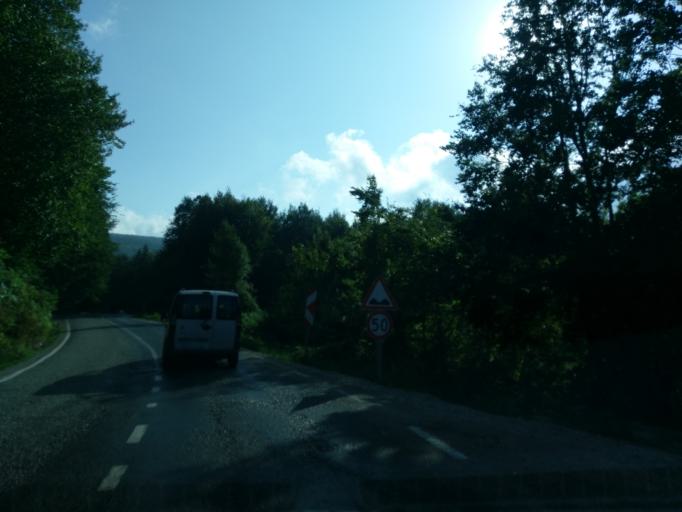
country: TR
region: Sinop
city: Ayancik
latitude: 41.8827
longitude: 34.5146
